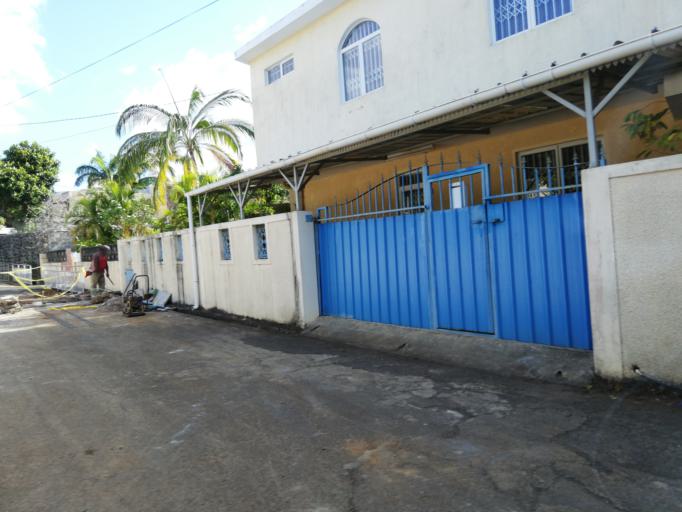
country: MU
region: Moka
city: Moka
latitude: -20.2256
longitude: 57.4728
